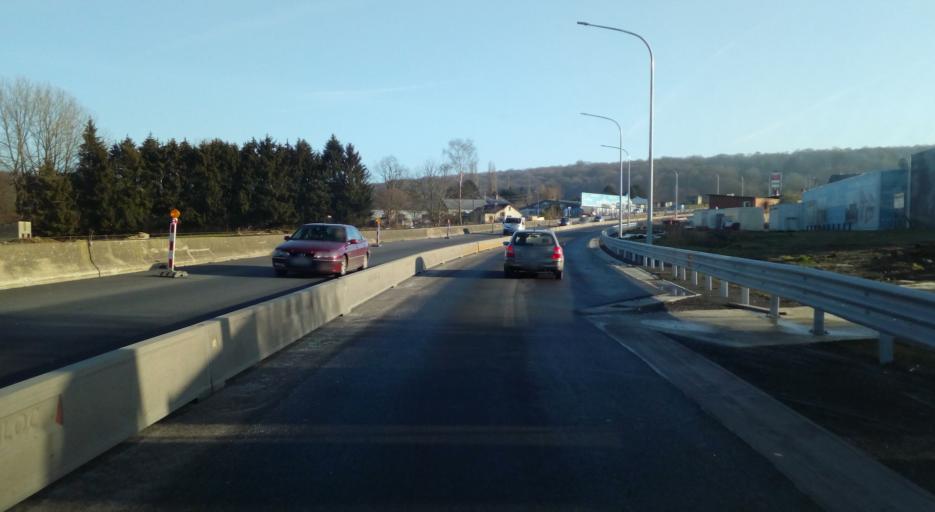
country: BE
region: Wallonia
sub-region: Province de Namur
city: Walcourt
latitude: 50.2782
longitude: 4.4986
